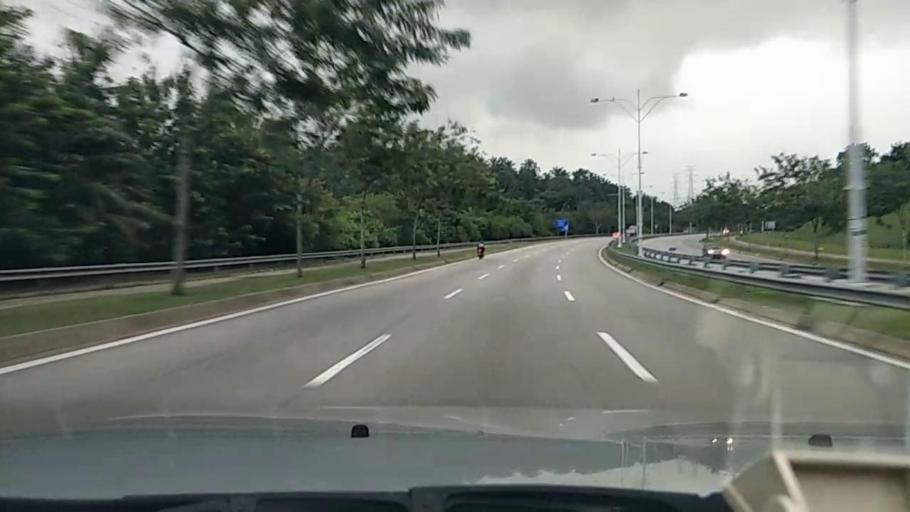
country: MY
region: Putrajaya
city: Putrajaya
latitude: 2.9484
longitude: 101.7132
